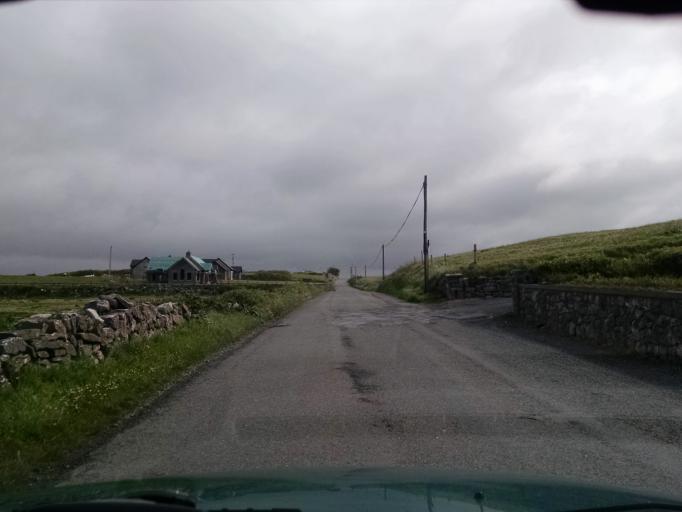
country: IE
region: Connaught
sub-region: County Galway
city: Bearna
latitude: 53.0341
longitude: -9.3619
